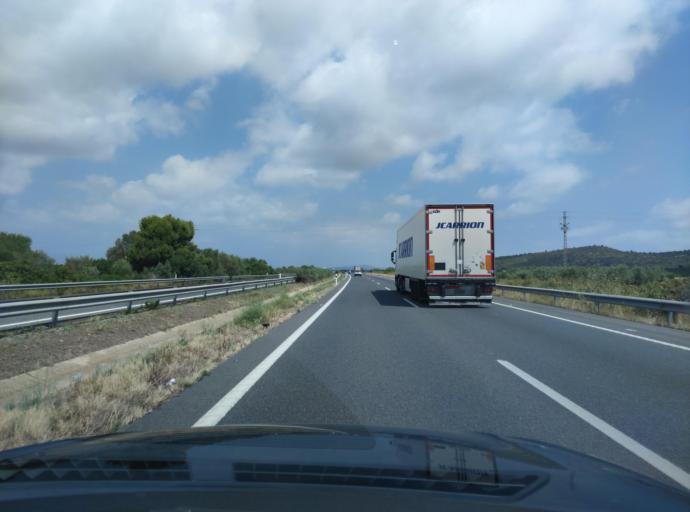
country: ES
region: Valencia
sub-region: Provincia de Castello
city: Vinaros
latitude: 40.4977
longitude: 0.4157
